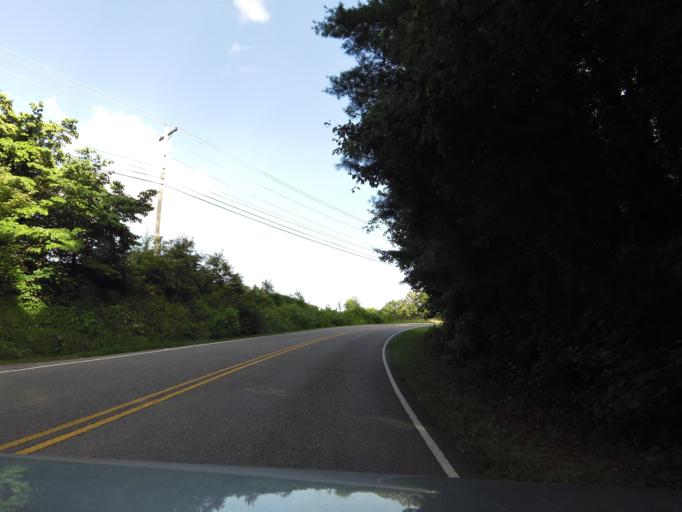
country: US
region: Tennessee
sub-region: Blount County
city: Eagleton Village
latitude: 35.8036
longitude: -83.9073
